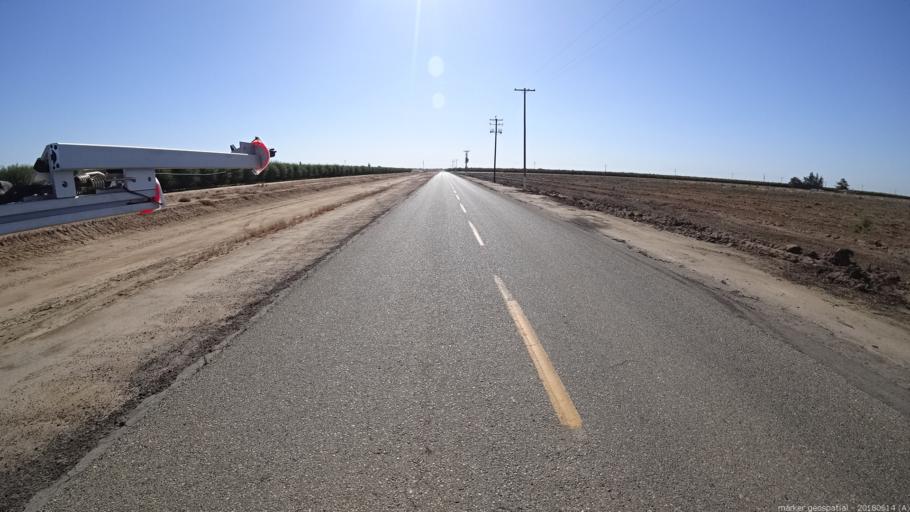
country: US
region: California
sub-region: Madera County
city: Madera
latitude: 36.9820
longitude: -120.1332
